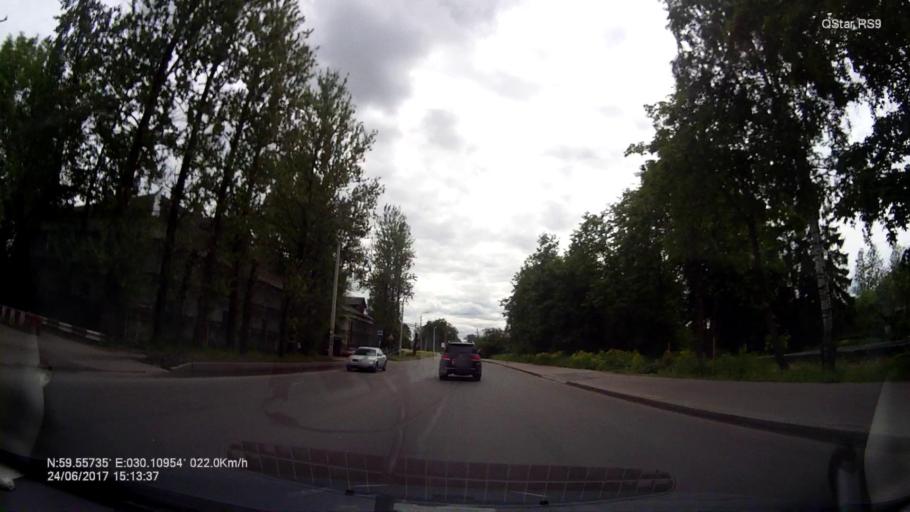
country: RU
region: Leningrad
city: Gatchina
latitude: 59.5573
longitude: 30.1095
